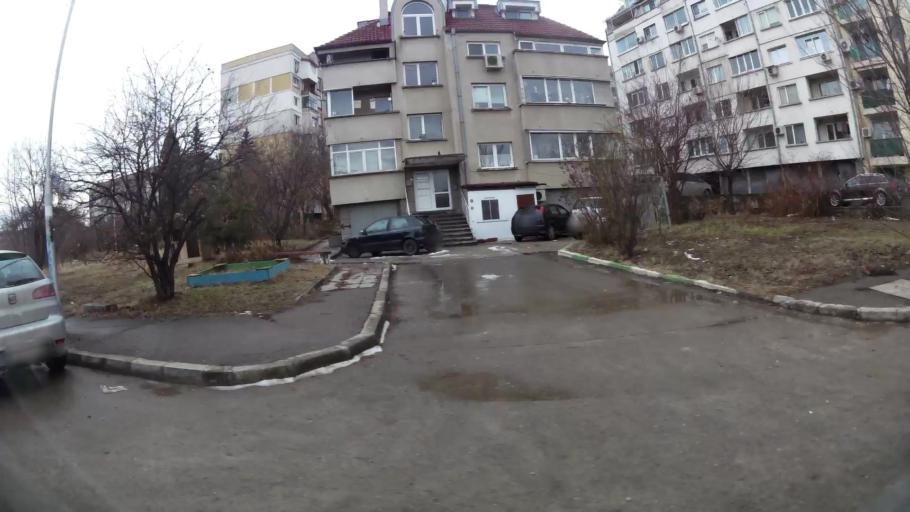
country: BG
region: Sofiya
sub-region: Obshtina Bozhurishte
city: Bozhurishte
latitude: 42.7268
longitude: 23.2579
